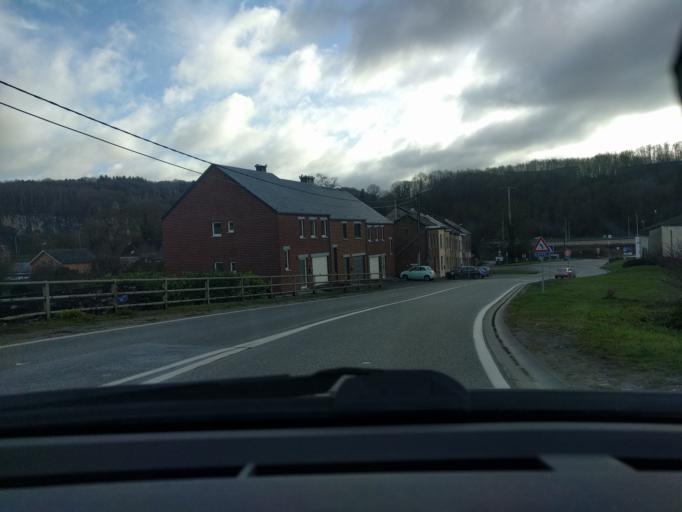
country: BE
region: Wallonia
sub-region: Province de Namur
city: Namur
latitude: 50.4676
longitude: 4.9194
